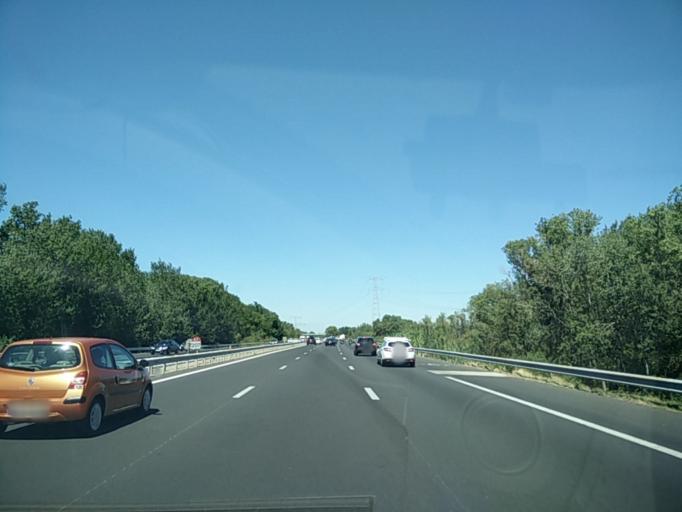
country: FR
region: Provence-Alpes-Cote d'Azur
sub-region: Departement des Bouches-du-Rhone
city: Cabannes
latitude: 43.8448
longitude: 4.9912
